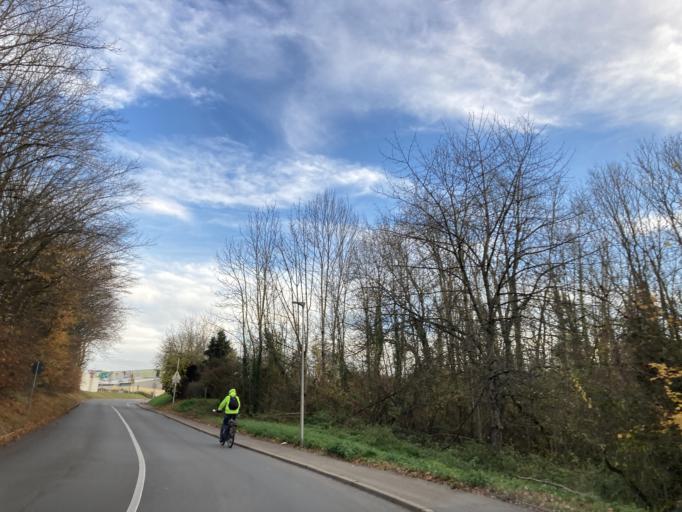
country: DE
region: Baden-Wuerttemberg
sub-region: Tuebingen Region
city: Rottenburg
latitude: 48.4688
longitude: 8.9257
